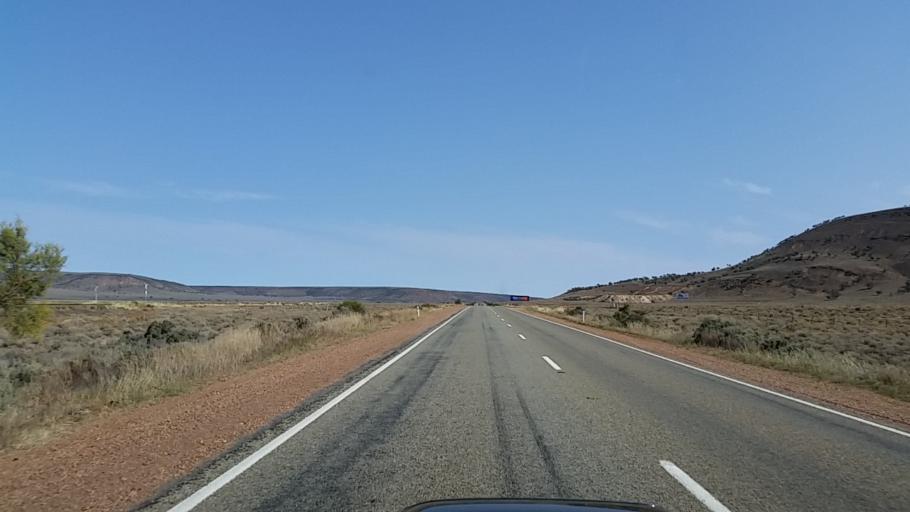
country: AU
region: South Australia
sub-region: Port Augusta
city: Port Augusta West
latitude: -32.5637
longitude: 137.6280
